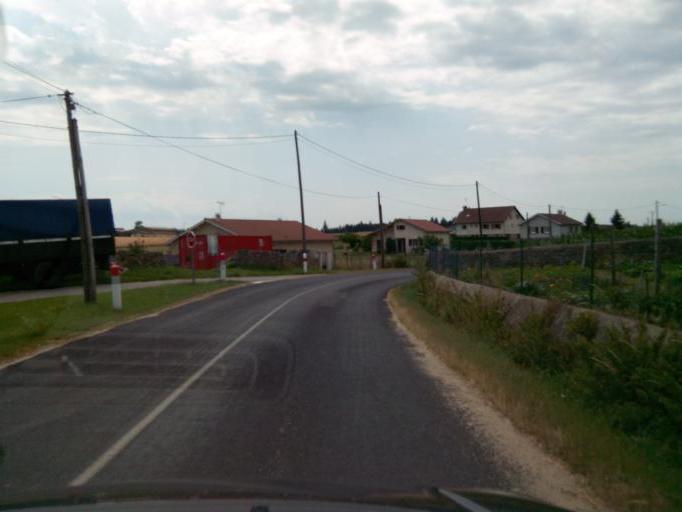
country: FR
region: Rhone-Alpes
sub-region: Departement de la Loire
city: Saint-Bonnet-le-Chateau
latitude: 45.3707
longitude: 4.0618
